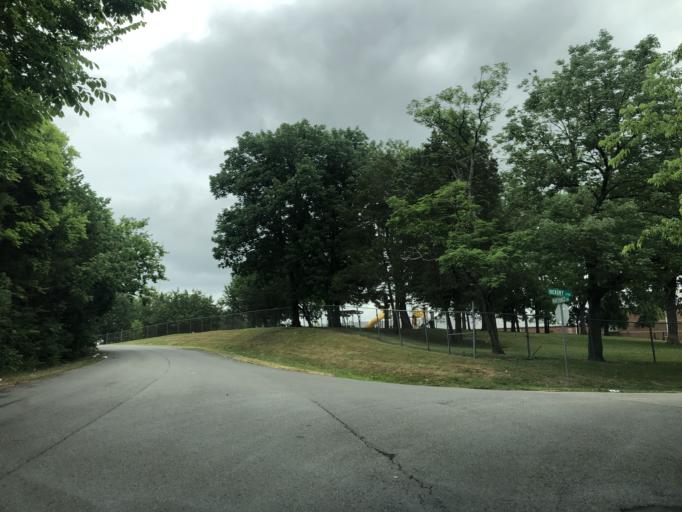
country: US
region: Tennessee
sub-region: Davidson County
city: Goodlettsville
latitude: 36.2710
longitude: -86.7634
